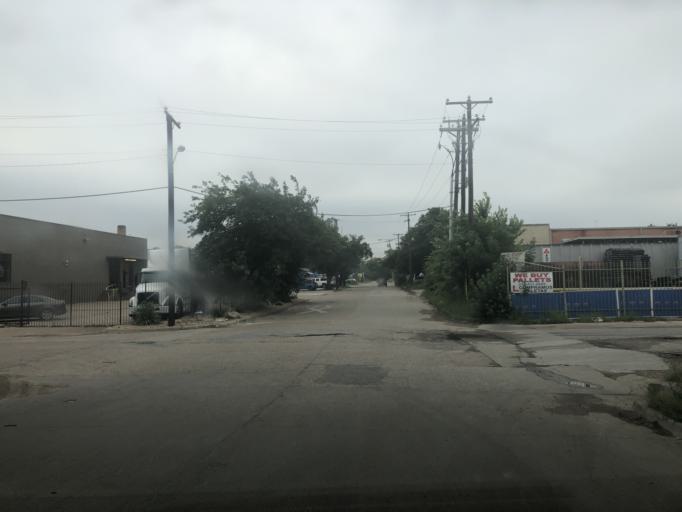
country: US
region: Texas
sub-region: Dallas County
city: Farmers Branch
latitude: 32.8633
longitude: -96.8787
